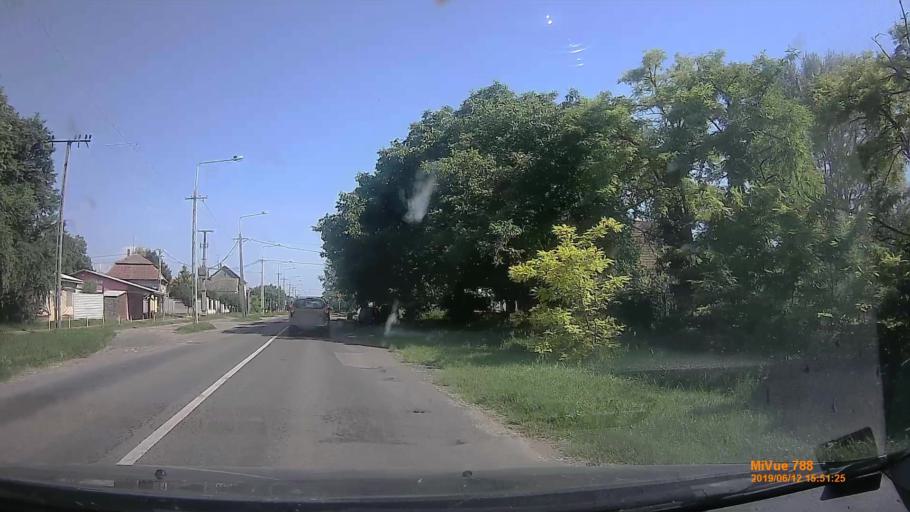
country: HU
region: Csongrad
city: Apatfalva
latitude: 46.1813
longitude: 20.5710
